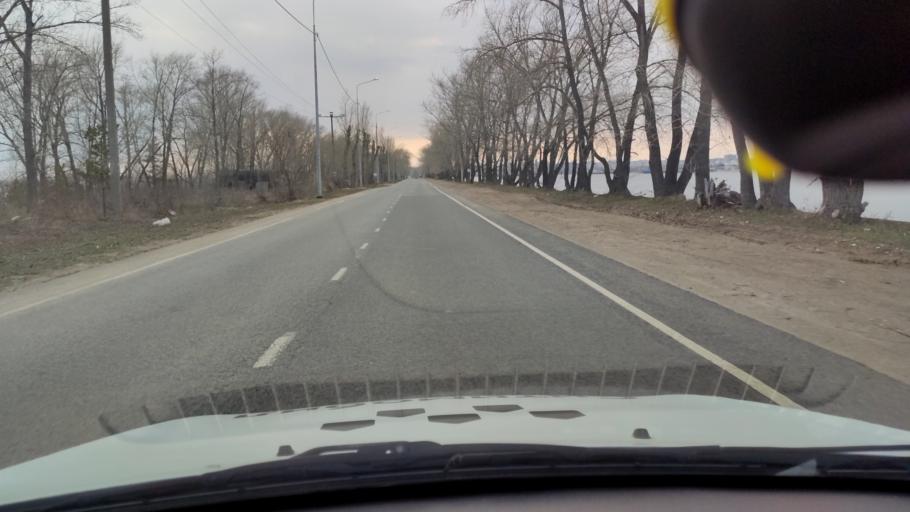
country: RU
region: Samara
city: Zhigulevsk
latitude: 53.4564
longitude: 49.5472
